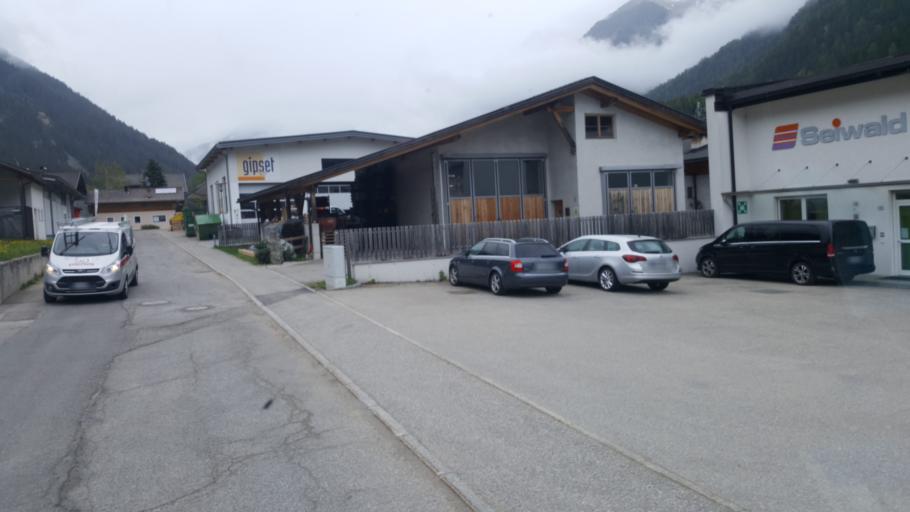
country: IT
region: Trentino-Alto Adige
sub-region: Bolzano
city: San Martino
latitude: 46.8017
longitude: 12.2147
